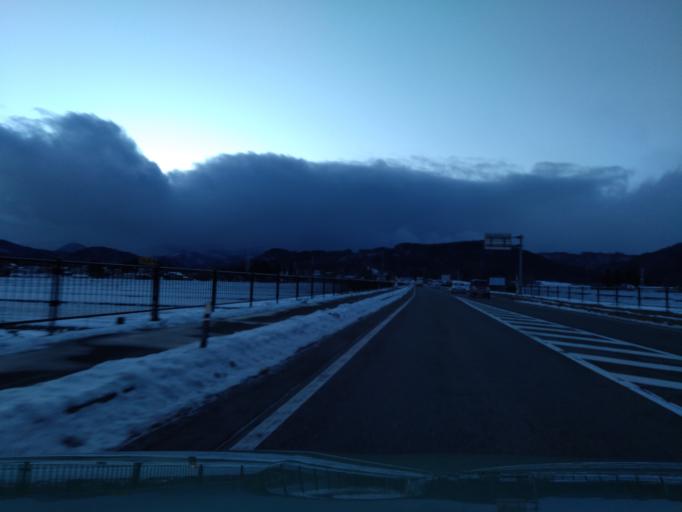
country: JP
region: Iwate
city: Shizukuishi
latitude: 39.6977
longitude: 140.9460
